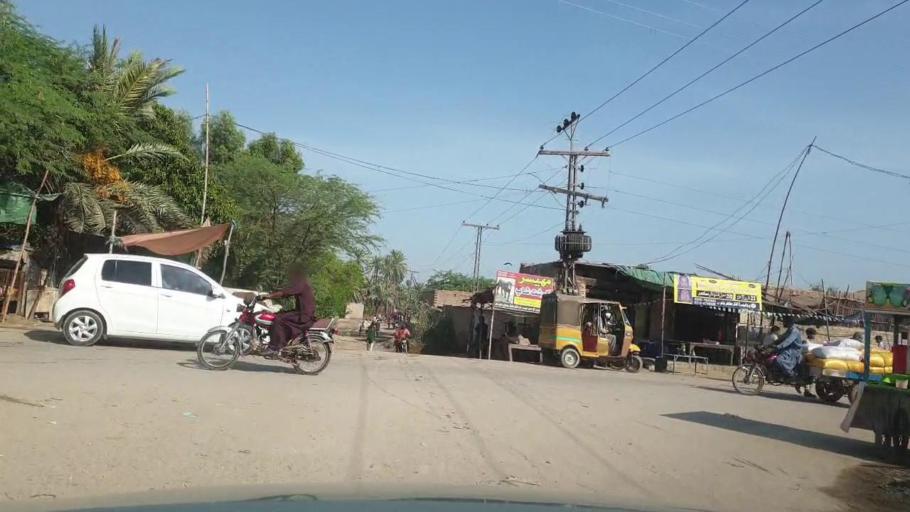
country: PK
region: Sindh
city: Rohri
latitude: 27.6789
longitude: 68.8795
